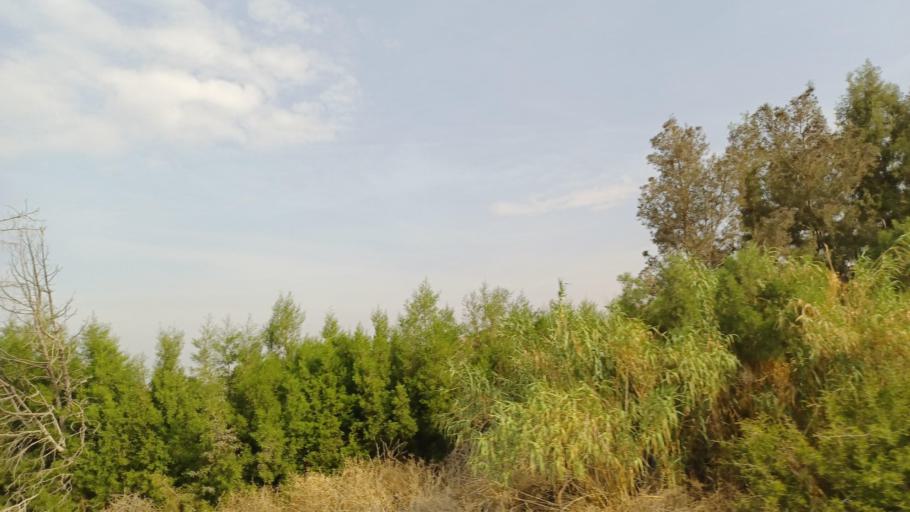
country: CY
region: Larnaka
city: Troulloi
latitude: 35.0034
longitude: 33.5729
